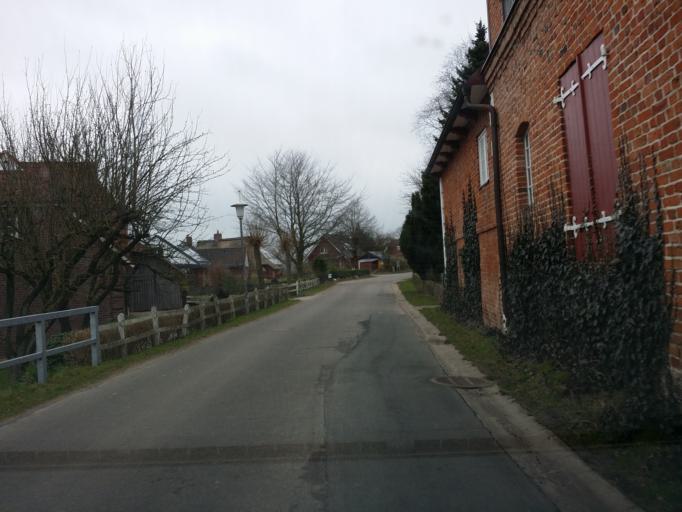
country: DE
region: Schleswig-Holstein
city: Bovenau
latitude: 54.3346
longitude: 9.8405
